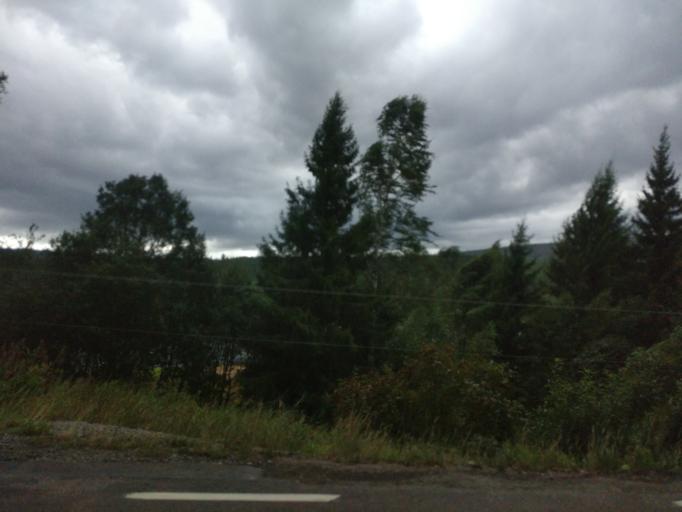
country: SE
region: Vaermland
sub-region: Torsby Kommun
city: Torsby
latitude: 60.6398
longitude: 13.0102
